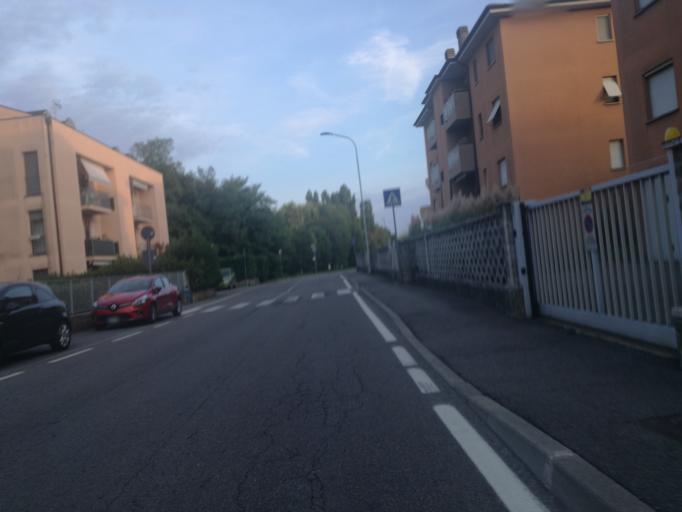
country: IT
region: Lombardy
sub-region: Provincia di Monza e Brianza
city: Porto d'Adda
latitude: 45.6502
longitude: 9.4696
